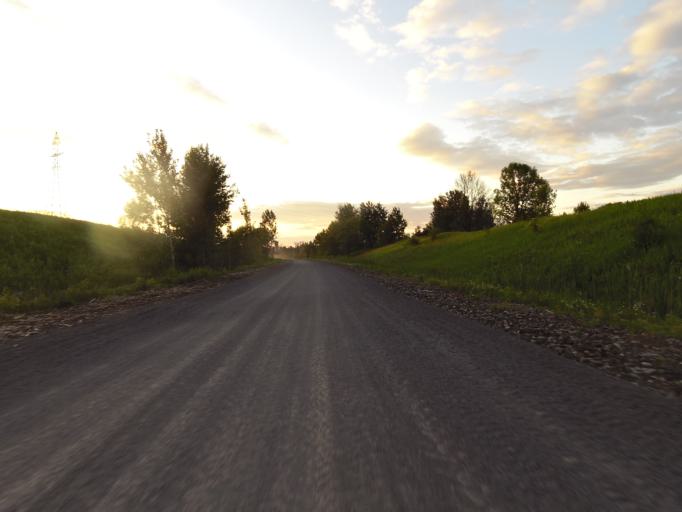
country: CA
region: Ontario
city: Arnprior
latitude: 45.3989
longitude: -76.3228
